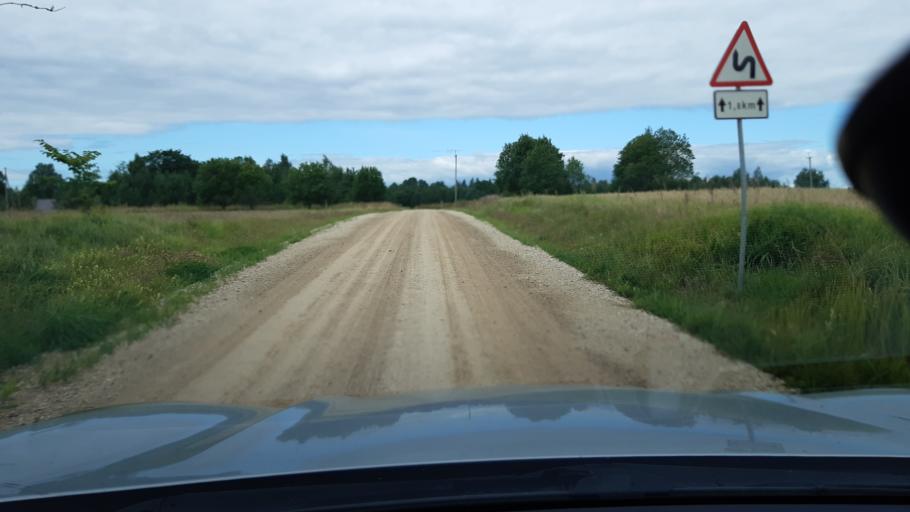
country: EE
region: Raplamaa
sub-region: Jaervakandi vald
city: Jarvakandi
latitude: 58.8050
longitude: 24.8472
